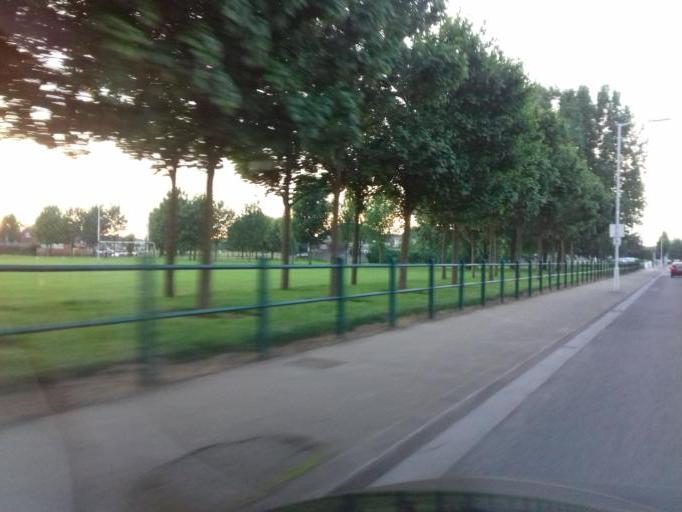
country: IE
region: Leinster
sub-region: Dublin City
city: Finglas
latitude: 53.3843
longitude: -6.3005
